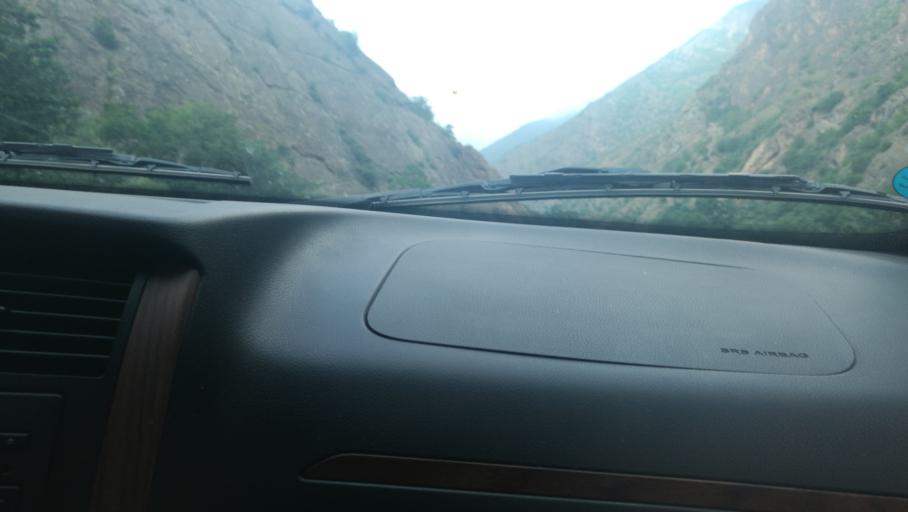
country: IR
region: Mazandaran
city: Chalus
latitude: 36.3193
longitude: 51.2503
